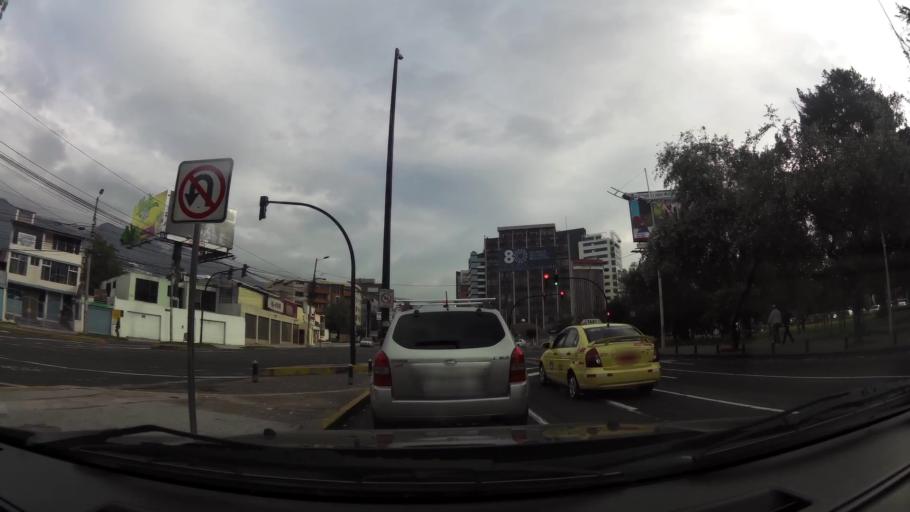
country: EC
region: Pichincha
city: Quito
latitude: -0.1879
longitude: -78.4874
